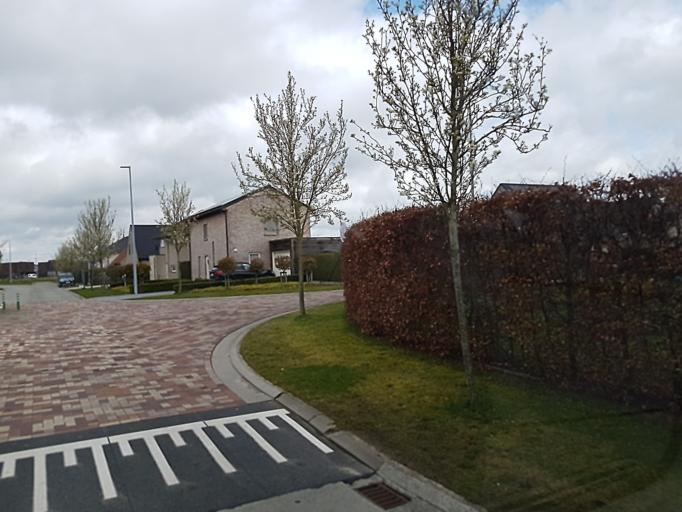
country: BE
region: Flanders
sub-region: Provincie Oost-Vlaanderen
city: Deinze
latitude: 50.9644
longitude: 3.5265
